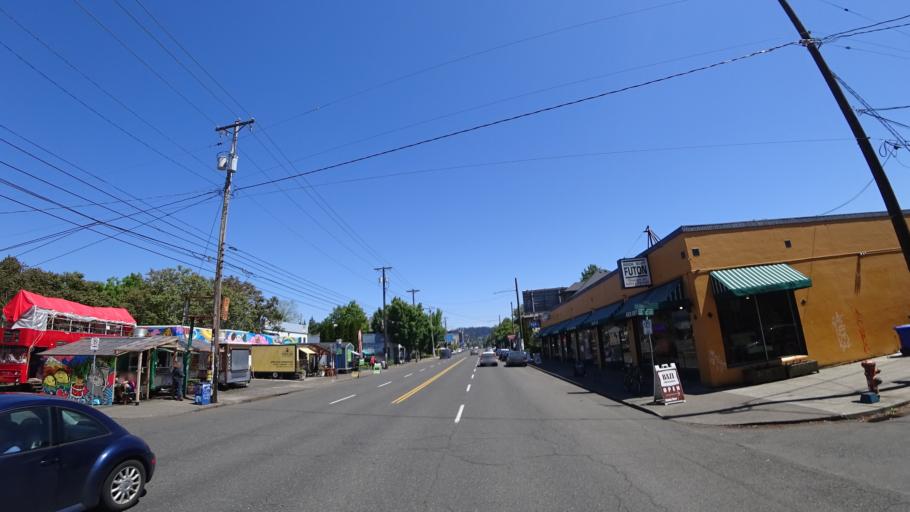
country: US
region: Oregon
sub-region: Multnomah County
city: Portland
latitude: 45.5120
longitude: -122.6328
